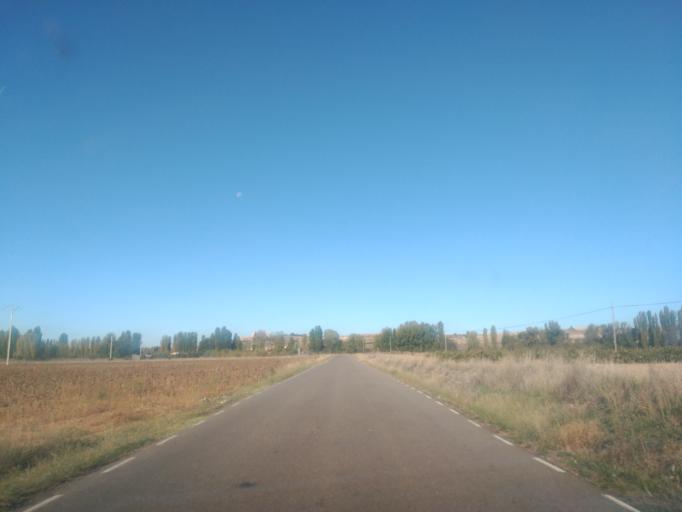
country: ES
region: Castille and Leon
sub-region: Provincia de Burgos
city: Penaranda de Duero
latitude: 41.6870
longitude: -3.4567
